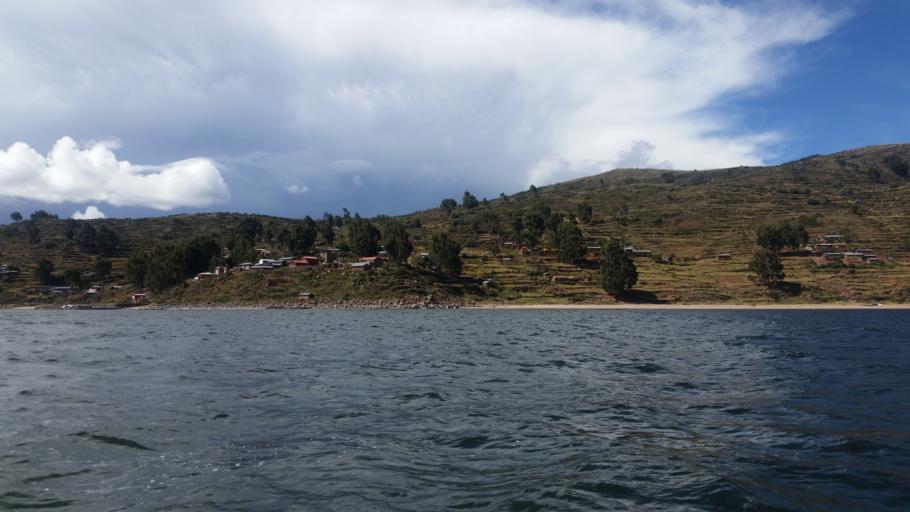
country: PE
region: Puno
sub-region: Provincia de Puno
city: Taquile
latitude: -15.7324
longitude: -69.7683
